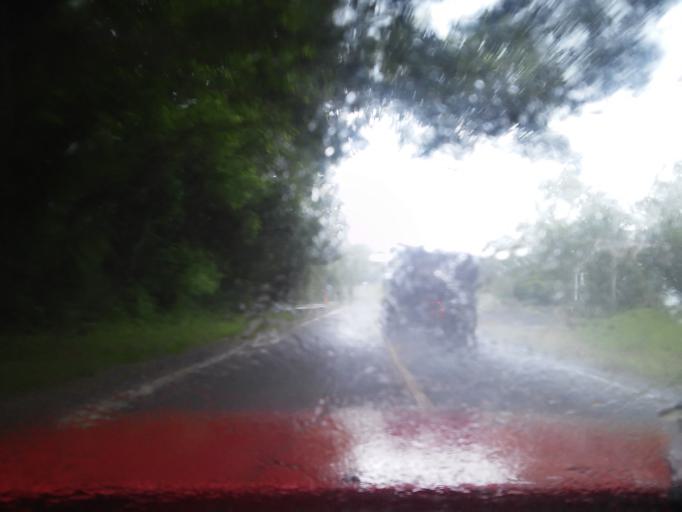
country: US
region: Virginia
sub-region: Montgomery County
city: Prices Fork
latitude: 37.3029
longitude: -80.4873
